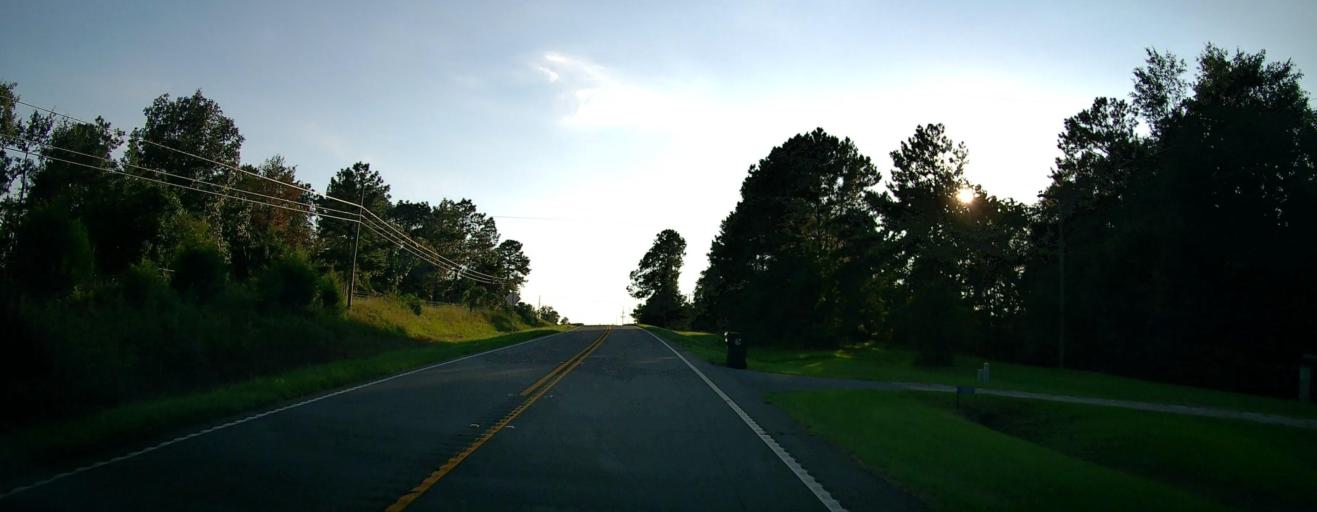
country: US
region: Georgia
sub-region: Crawford County
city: Roberta
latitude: 32.6987
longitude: -84.0486
